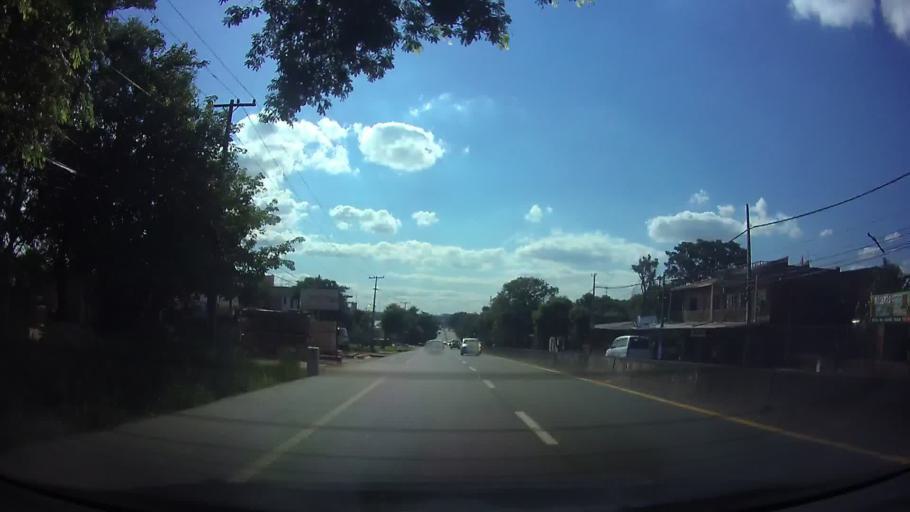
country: PY
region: Central
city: Itaugua
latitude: -25.3980
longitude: -57.3351
